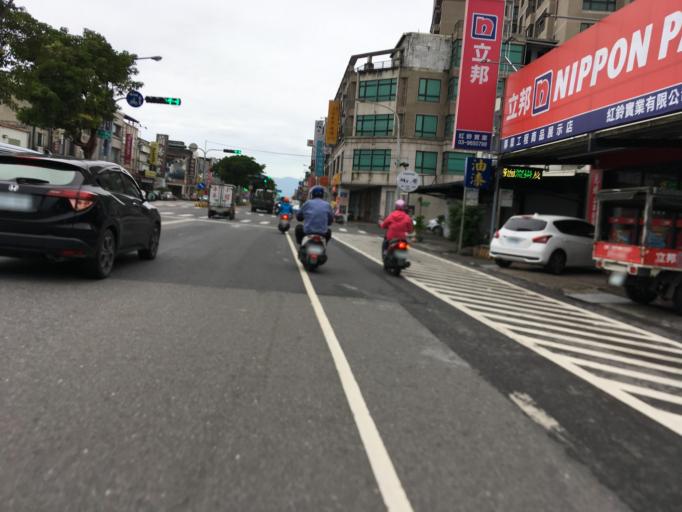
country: TW
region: Taiwan
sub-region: Yilan
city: Yilan
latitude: 24.6898
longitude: 121.7704
